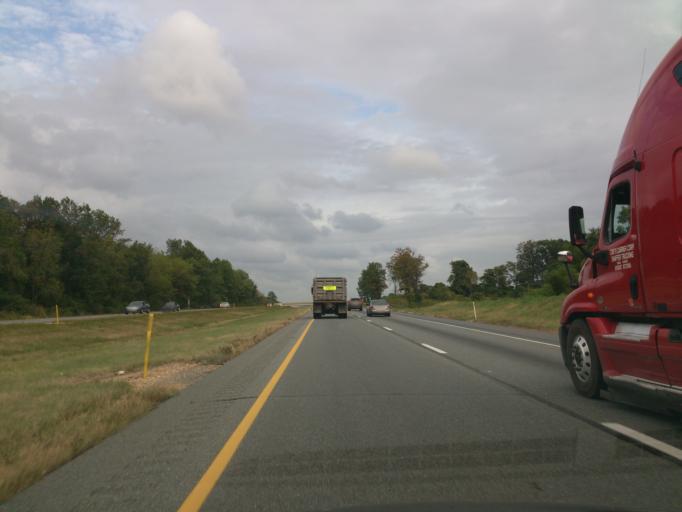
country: US
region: Pennsylvania
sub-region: Lancaster County
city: Reamstown
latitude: 40.2077
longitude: -76.1121
